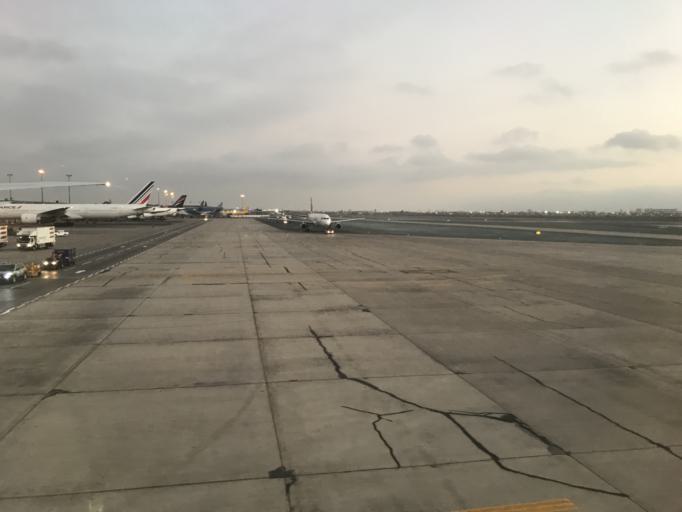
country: PE
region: Callao
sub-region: Callao
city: Callao
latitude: -12.0240
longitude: -77.1100
